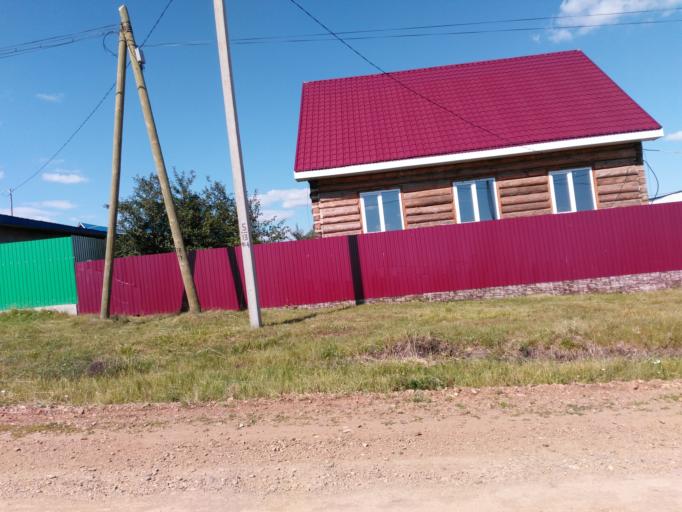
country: RU
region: Bashkortostan
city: Uchaly
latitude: 54.2927
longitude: 59.3649
